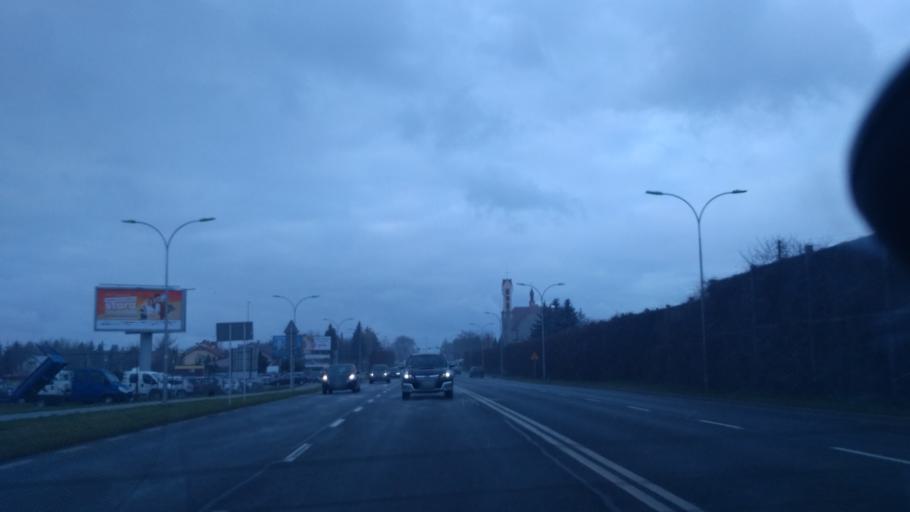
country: PL
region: Subcarpathian Voivodeship
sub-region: Powiat rzeszowski
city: Krasne
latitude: 50.0392
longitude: 22.0506
